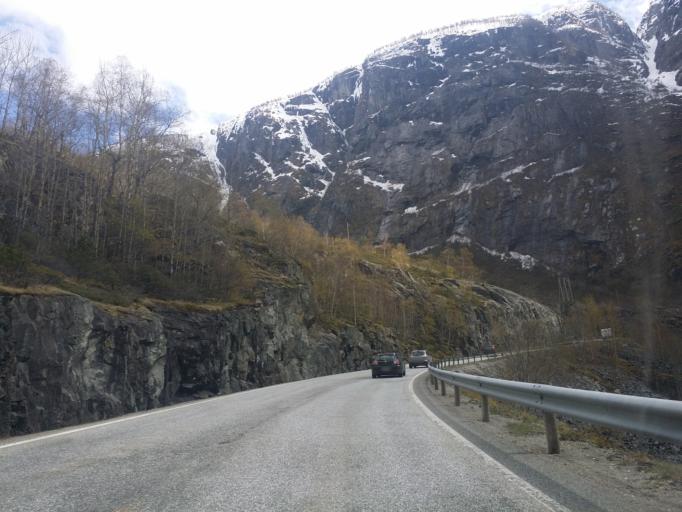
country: NO
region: Hordaland
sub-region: Eidfjord
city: Eidfjord
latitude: 60.4193
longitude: 7.1915
